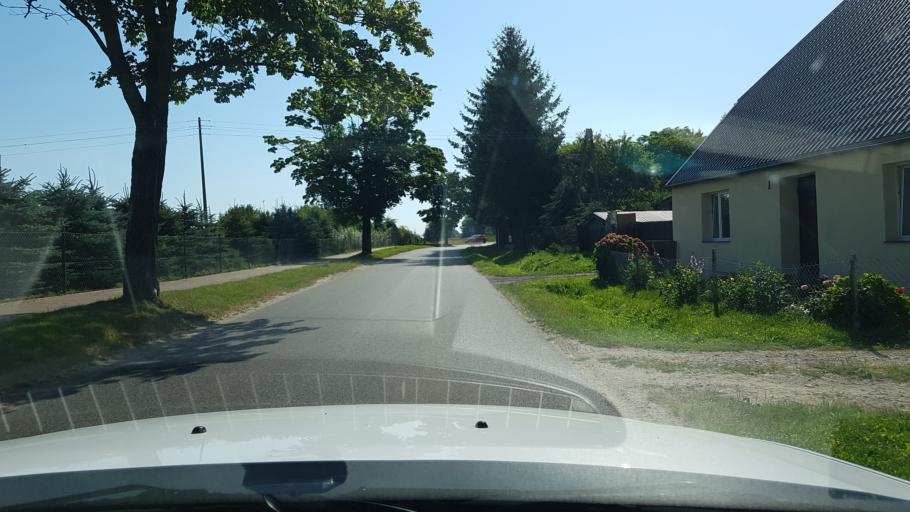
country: PL
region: West Pomeranian Voivodeship
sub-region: Powiat koszalinski
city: Sianow
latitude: 54.2669
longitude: 16.2407
